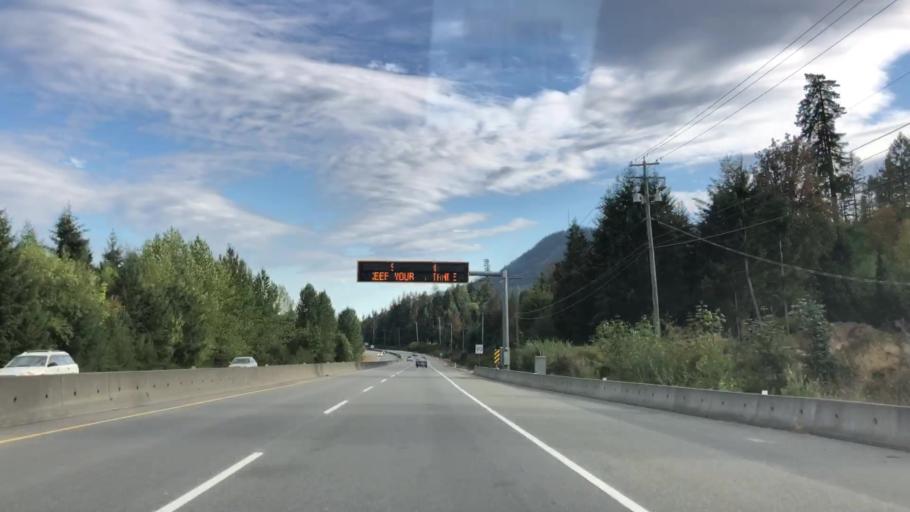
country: CA
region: British Columbia
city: North Saanich
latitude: 48.6253
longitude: -123.5474
